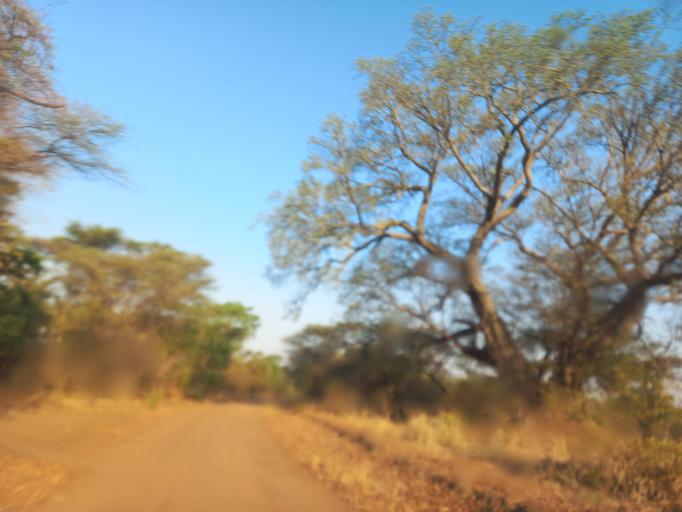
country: ZM
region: Lusaka
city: Luangwa
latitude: -15.4288
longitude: 30.3338
